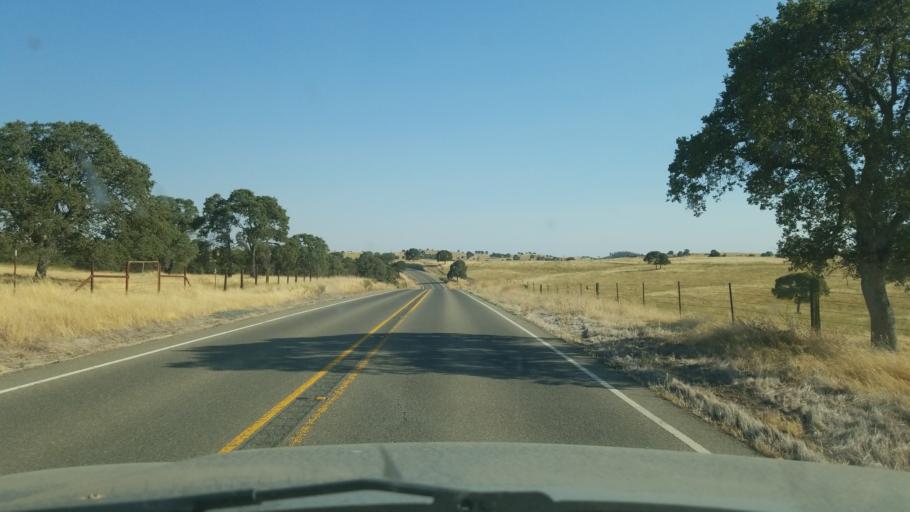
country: US
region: California
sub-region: Tuolumne County
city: Jamestown
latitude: 37.8079
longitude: -120.4728
